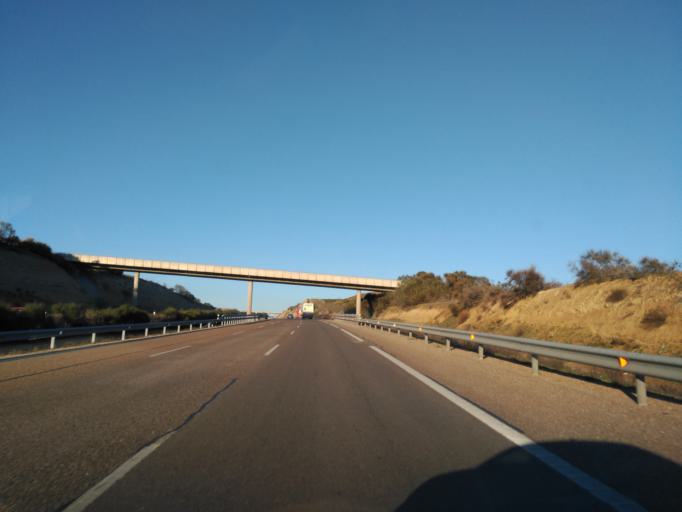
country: ES
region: Castille and Leon
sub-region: Provincia de Zamora
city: Castrillo de la Guarena
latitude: 41.2373
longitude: -5.3044
